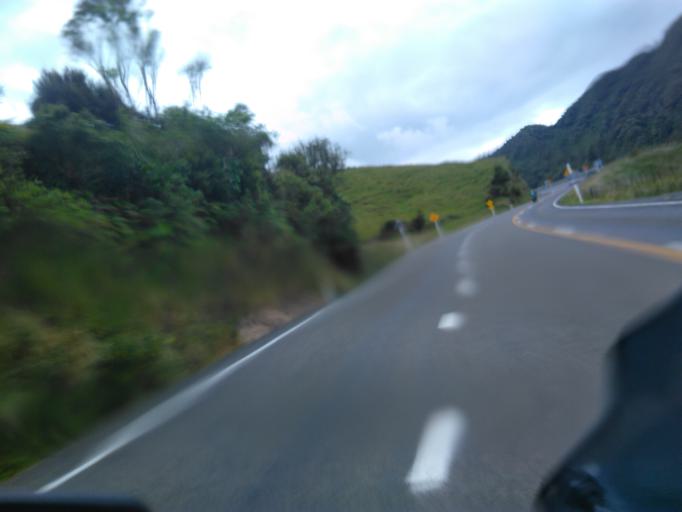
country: NZ
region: Bay of Plenty
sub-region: Opotiki District
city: Opotiki
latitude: -38.3526
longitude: 177.4508
